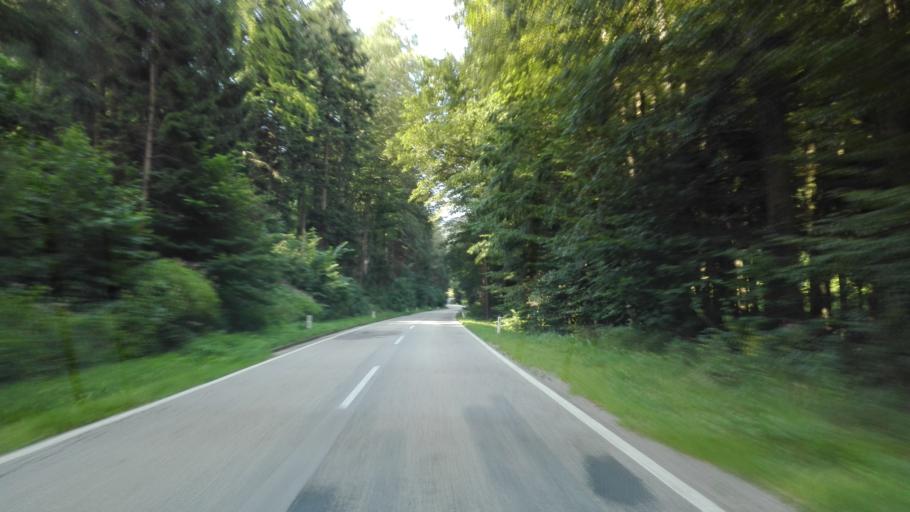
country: AT
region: Lower Austria
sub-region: Politischer Bezirk Sankt Polten
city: Stossing
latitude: 48.0858
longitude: 15.7812
